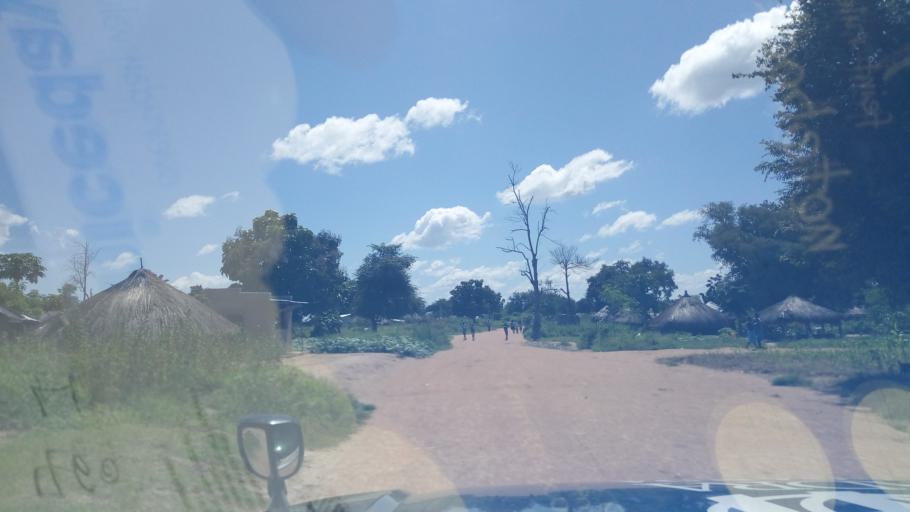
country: UG
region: Northern Region
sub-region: Arua District
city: Arua
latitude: 3.0768
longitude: 31.2834
